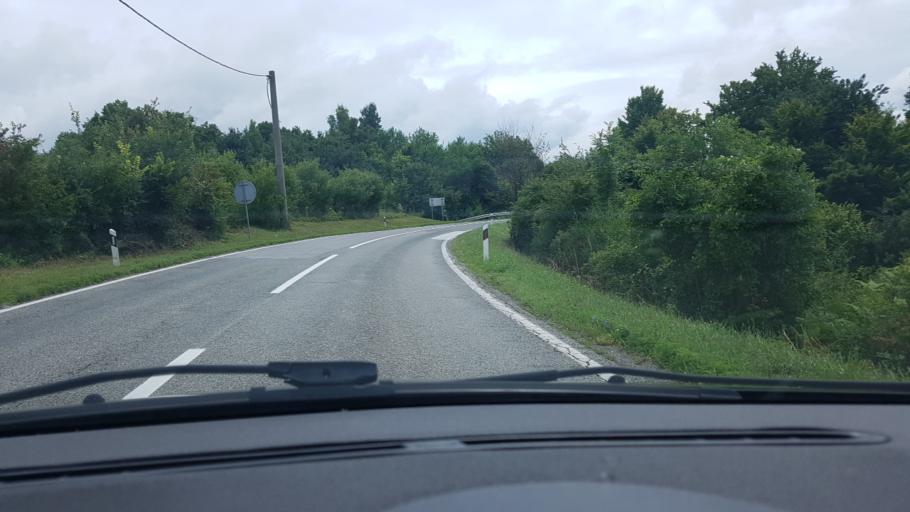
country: HR
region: Licko-Senjska
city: Jezerce
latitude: 44.9460
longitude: 15.6781
